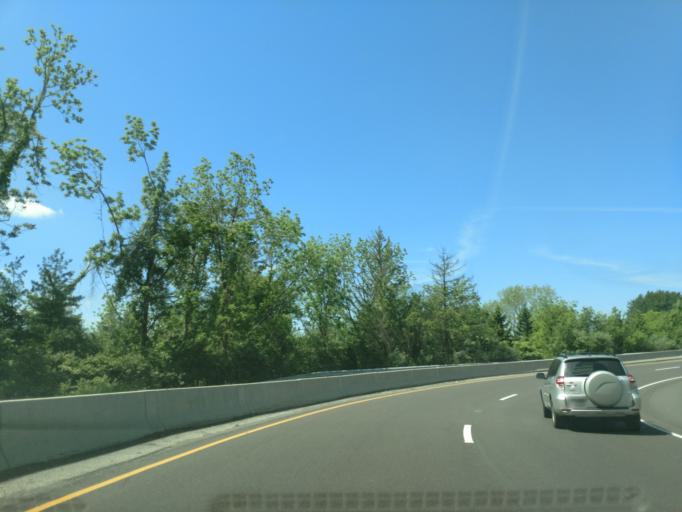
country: US
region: Pennsylvania
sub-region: Montgomery County
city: King of Prussia
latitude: 40.0939
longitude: -75.4191
